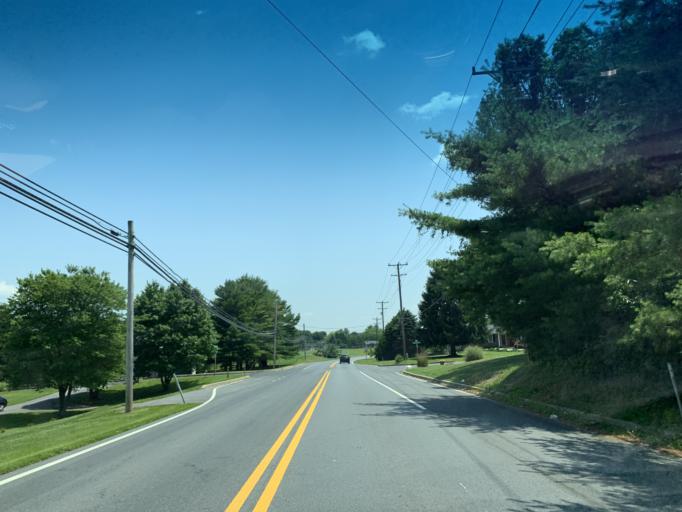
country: US
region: Maryland
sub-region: Frederick County
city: Green Valley
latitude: 39.3644
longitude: -77.2699
